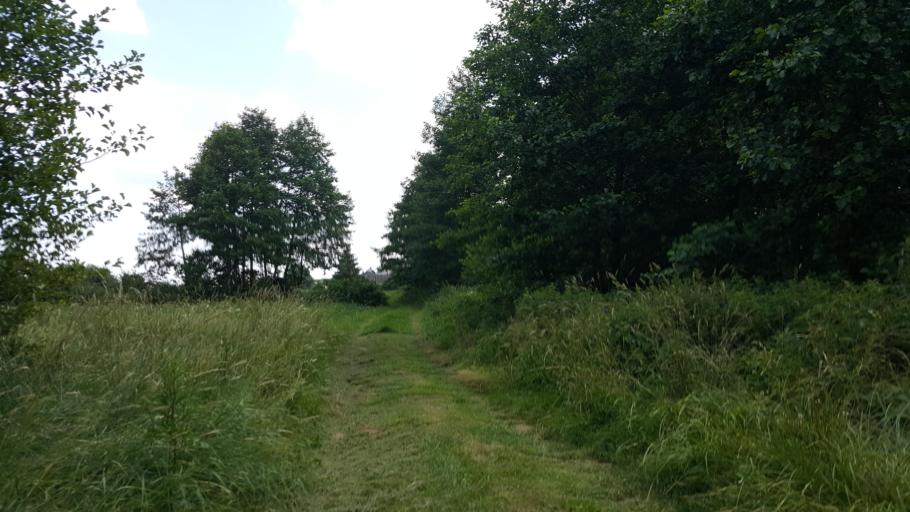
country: BY
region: Brest
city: Kamyanyets
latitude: 52.4047
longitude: 23.7852
